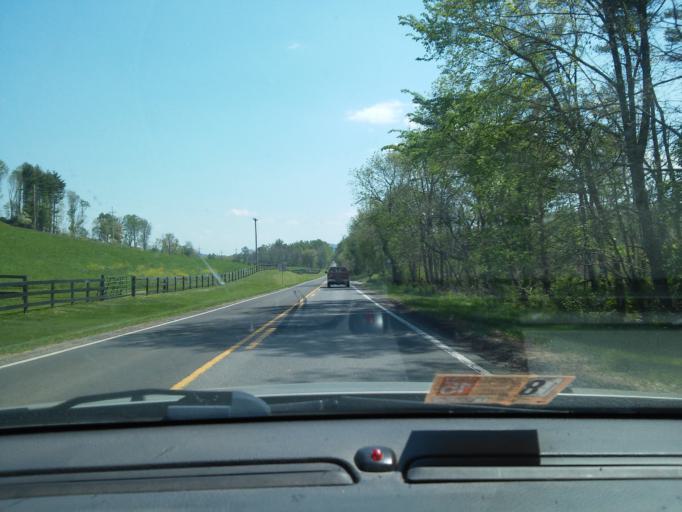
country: US
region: Virginia
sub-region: Warren County
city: Apple Mountain Lake
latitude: 38.8141
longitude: -78.1063
